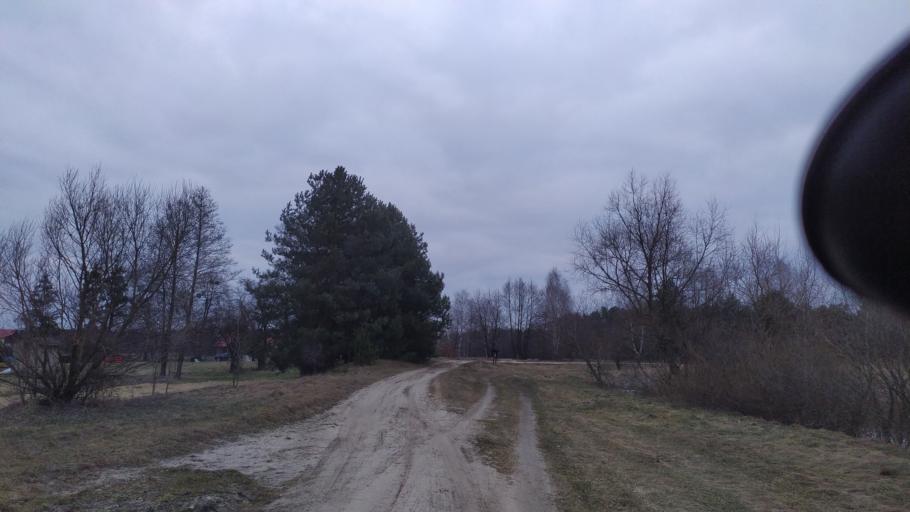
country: PL
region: Lublin Voivodeship
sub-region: Powiat lubartowski
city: Abramow
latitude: 51.4250
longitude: 22.2884
